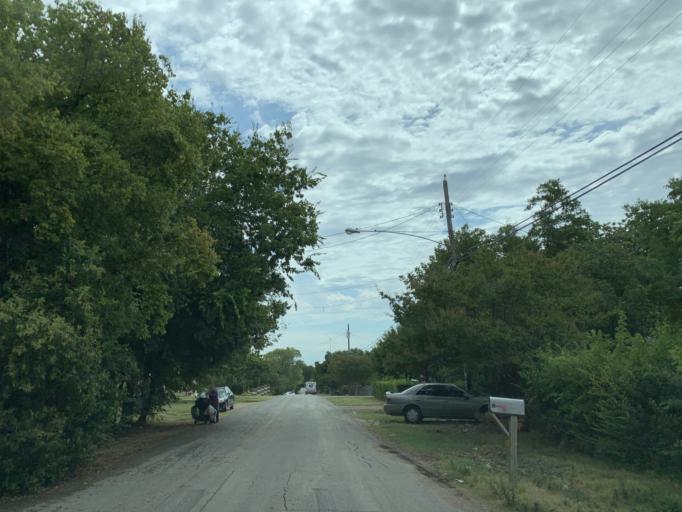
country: US
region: Texas
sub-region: Dallas County
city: Duncanville
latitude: 32.6712
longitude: -96.8308
